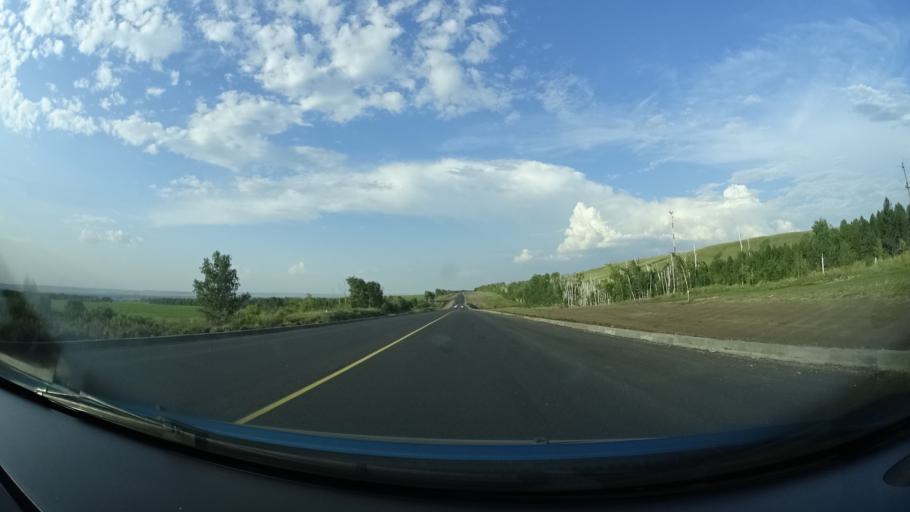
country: RU
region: Samara
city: Sukhodol
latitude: 53.7600
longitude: 50.8803
